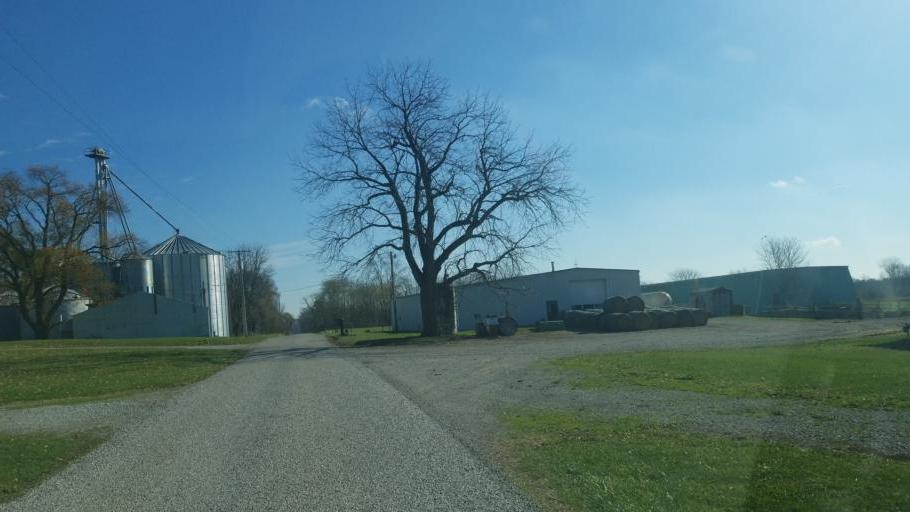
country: US
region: Ohio
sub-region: Ashland County
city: Ashland
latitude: 40.9219
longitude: -82.3074
